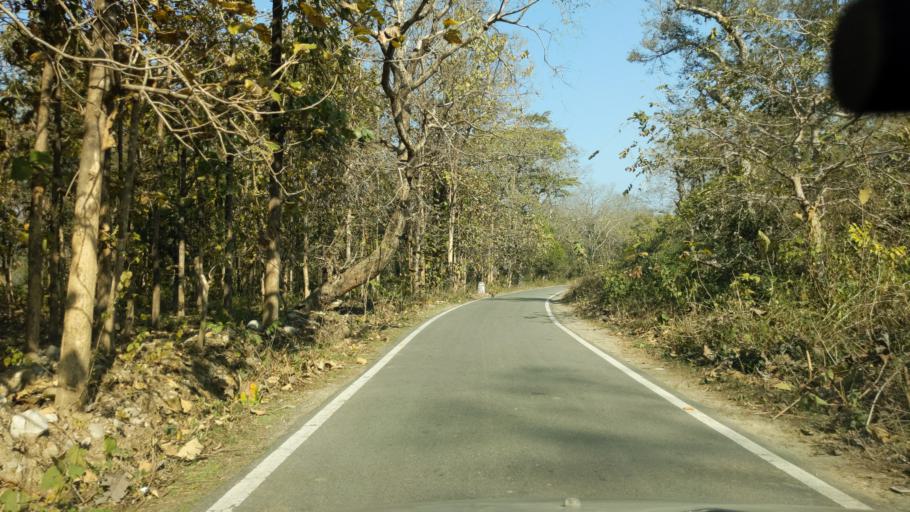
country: IN
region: Uttarakhand
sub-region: Naini Tal
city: Ramnagar
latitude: 29.4149
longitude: 79.1371
